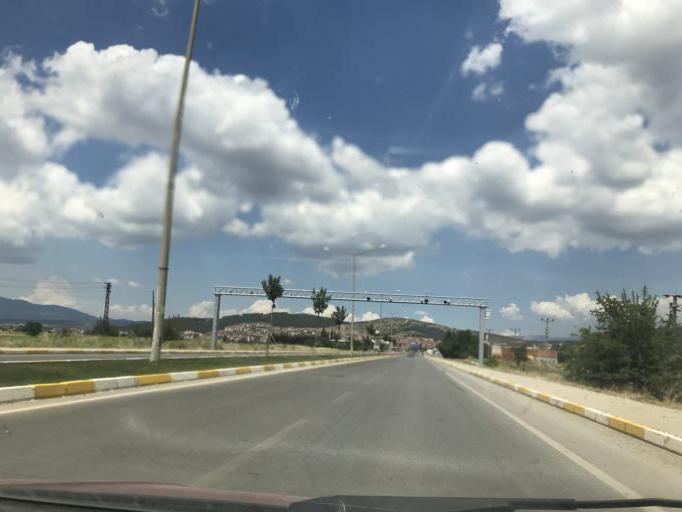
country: TR
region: Denizli
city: Tavas
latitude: 37.5581
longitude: 29.0577
